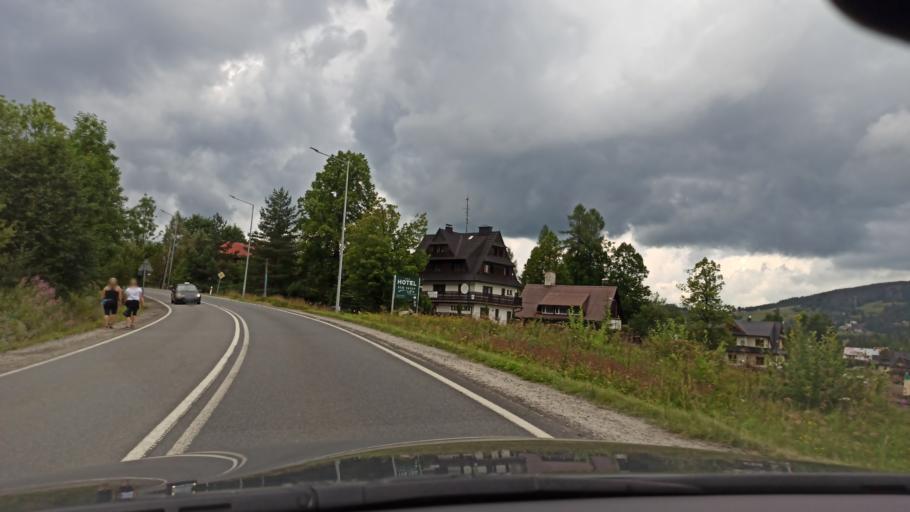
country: PL
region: Lesser Poland Voivodeship
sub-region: Powiat tatrzanski
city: Koscielisko
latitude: 49.2762
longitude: 19.8876
